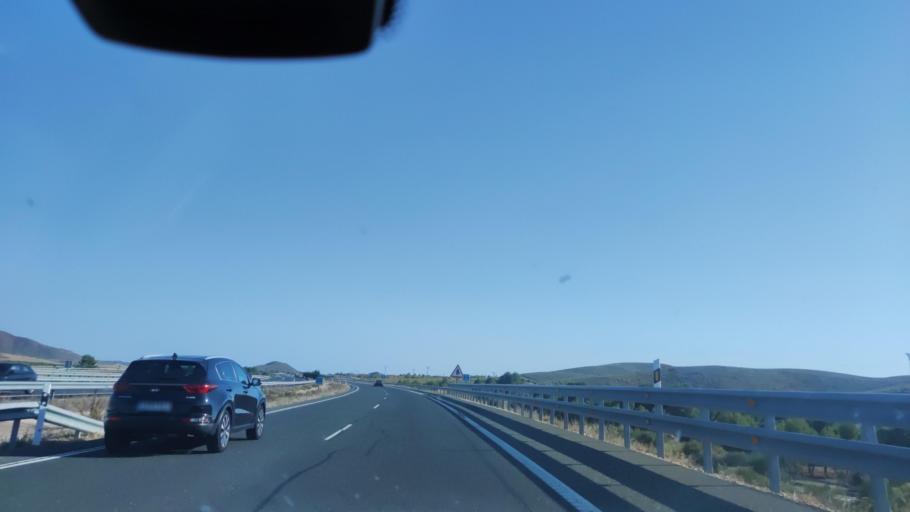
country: ES
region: Castille-La Mancha
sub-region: Provincia de Albacete
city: Tobarra
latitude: 38.5763
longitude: -1.6882
